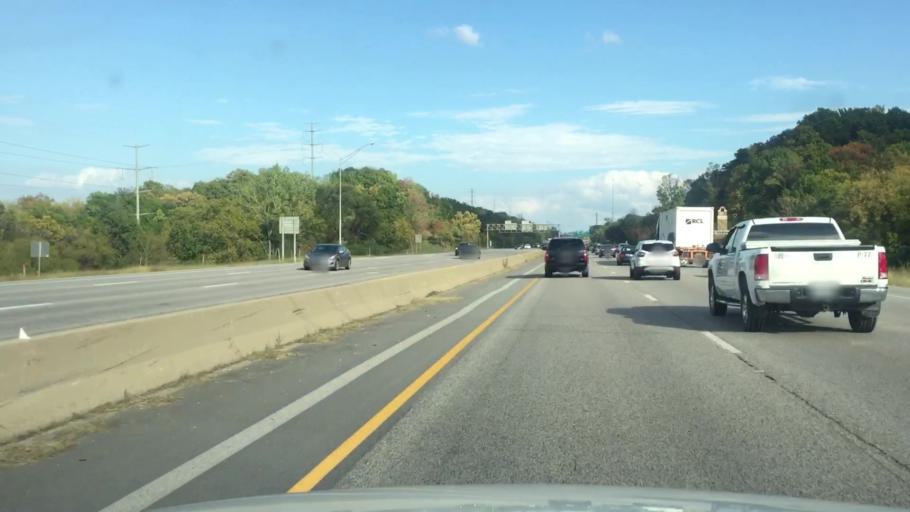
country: US
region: Missouri
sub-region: Jackson County
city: Lees Summit
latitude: 38.9360
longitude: -94.4463
